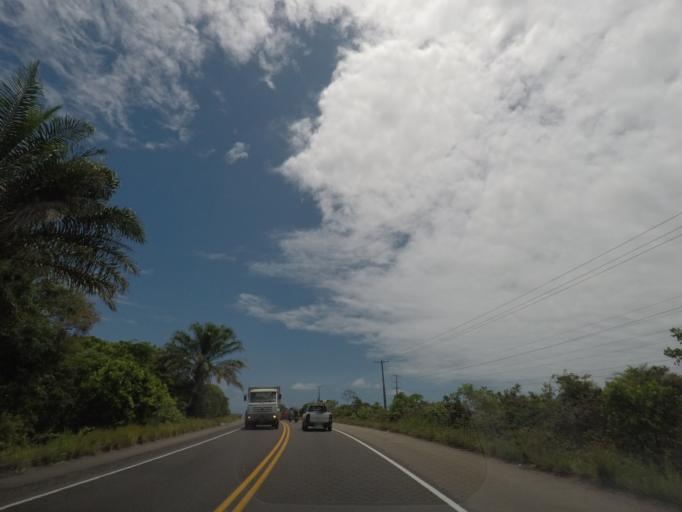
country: BR
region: Bahia
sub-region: Itaparica
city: Itaparica
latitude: -12.9746
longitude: -38.6355
